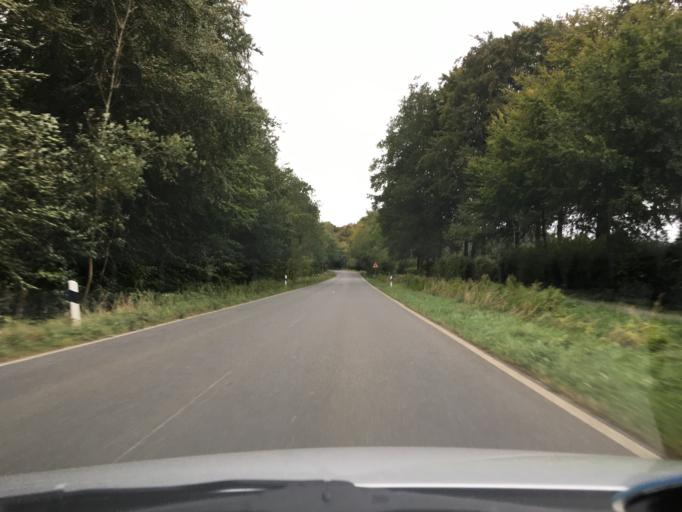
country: DE
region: Schleswig-Holstein
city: Danischenhagen
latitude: 54.4792
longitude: 10.1082
